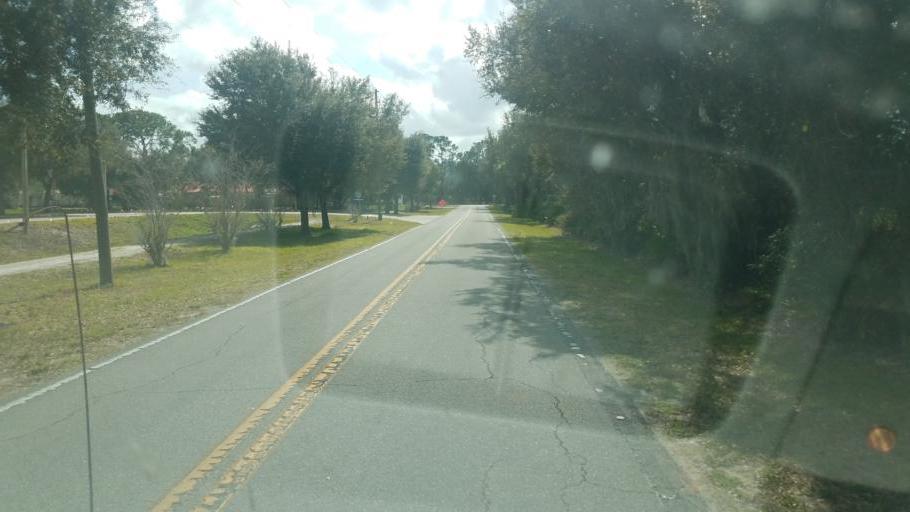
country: US
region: Florida
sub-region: Osceola County
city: Poinciana
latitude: 27.9736
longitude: -81.3820
